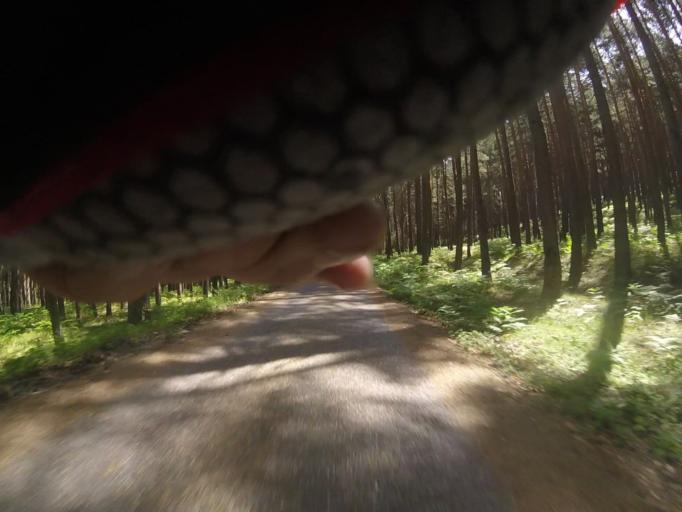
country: ES
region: Madrid
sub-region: Provincia de Madrid
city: Cercedilla
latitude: 40.8130
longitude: -4.0309
